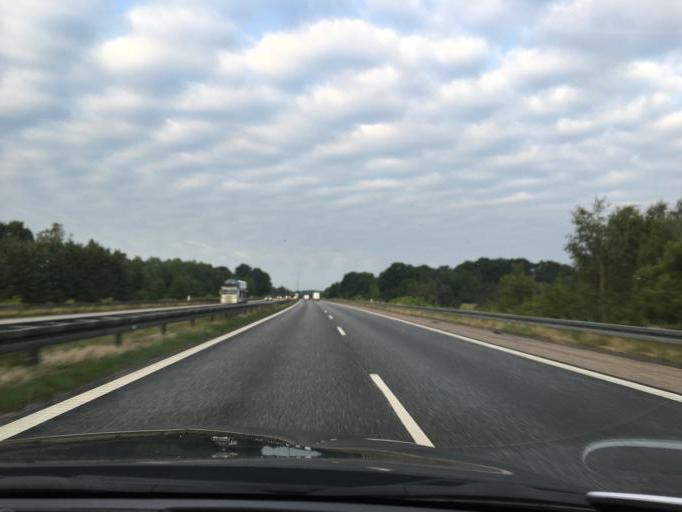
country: DK
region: Zealand
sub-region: Soro Kommune
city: Soro
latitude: 55.4499
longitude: 11.5254
